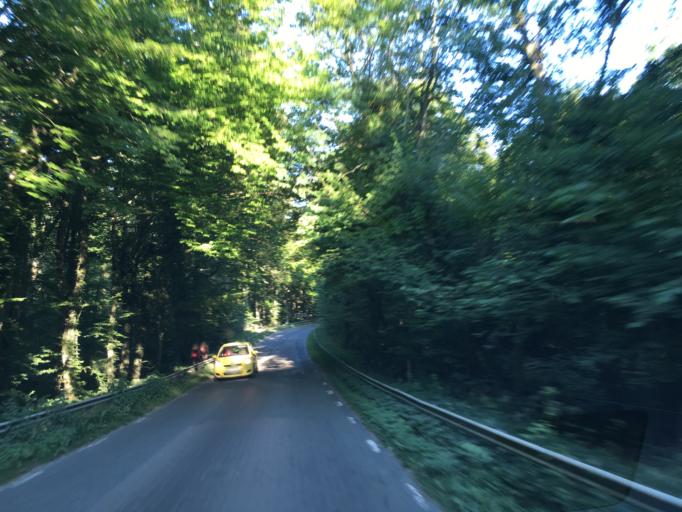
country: SE
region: Skane
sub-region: Simrishamns Kommun
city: Kivik
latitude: 55.6571
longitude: 14.2658
